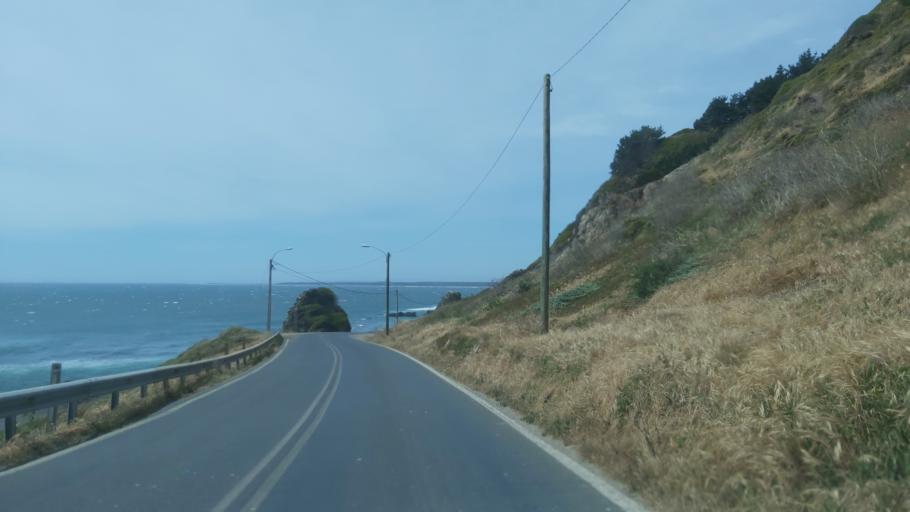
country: CL
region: Maule
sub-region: Provincia de Talca
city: Constitucion
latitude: -35.3302
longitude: -72.4331
